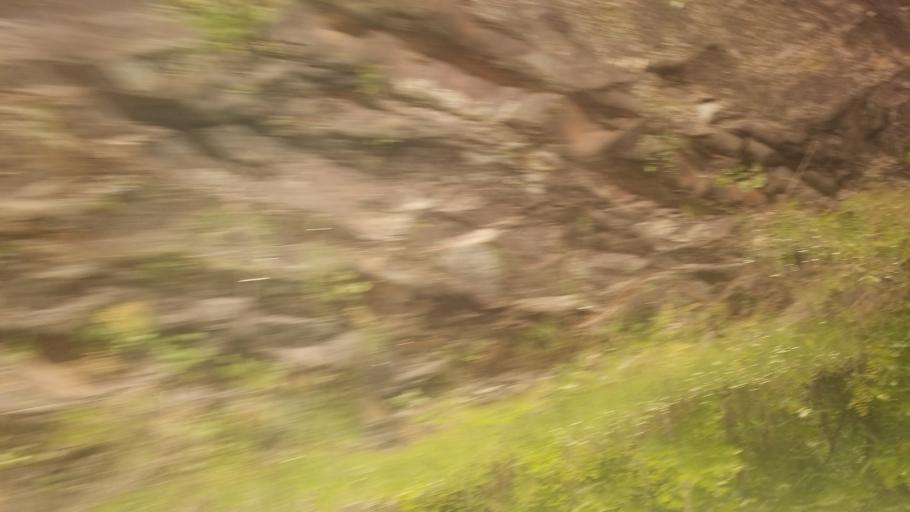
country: US
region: West Virginia
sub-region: Morgan County
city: Berkeley Springs
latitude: 39.5967
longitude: -78.3994
